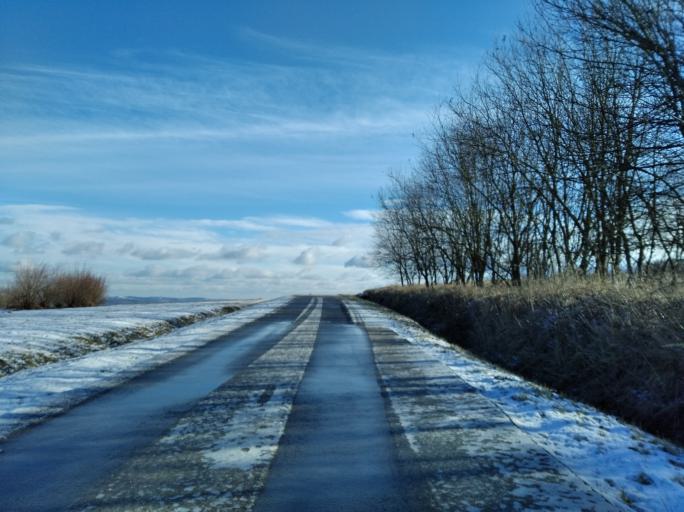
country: PL
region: Subcarpathian Voivodeship
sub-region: Powiat ropczycko-sedziszowski
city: Wielopole Skrzynskie
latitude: 49.9107
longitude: 21.6405
